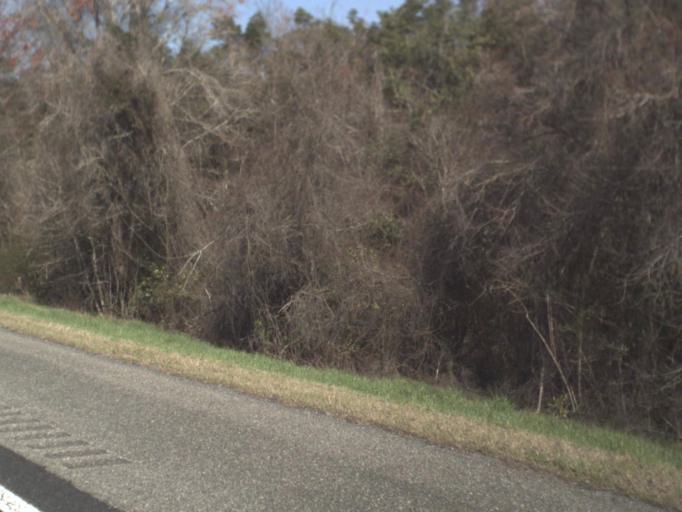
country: US
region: Florida
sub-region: Gadsden County
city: Gretna
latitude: 30.5747
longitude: -84.6872
